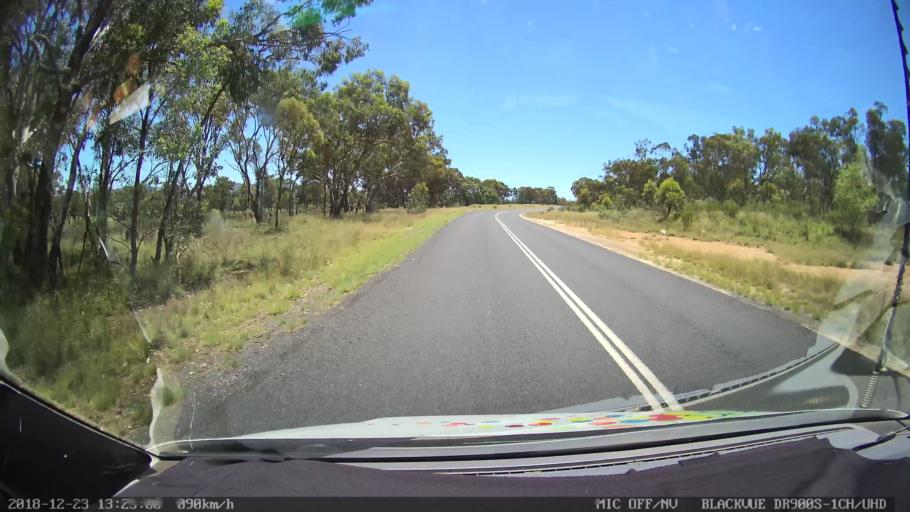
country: AU
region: New South Wales
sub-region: Armidale Dumaresq
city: Armidale
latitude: -30.4763
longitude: 151.3820
